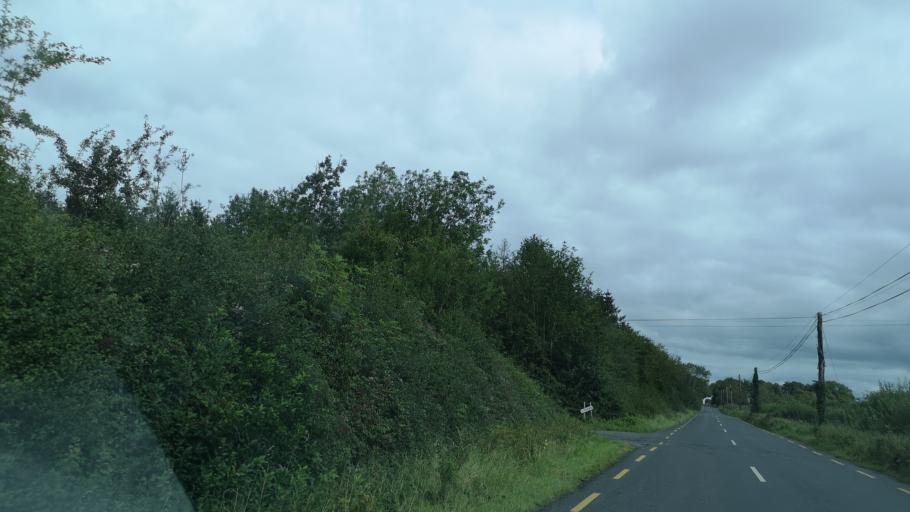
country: IE
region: Leinster
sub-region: Uibh Fhaili
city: Ferbane
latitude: 53.2293
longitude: -7.7850
